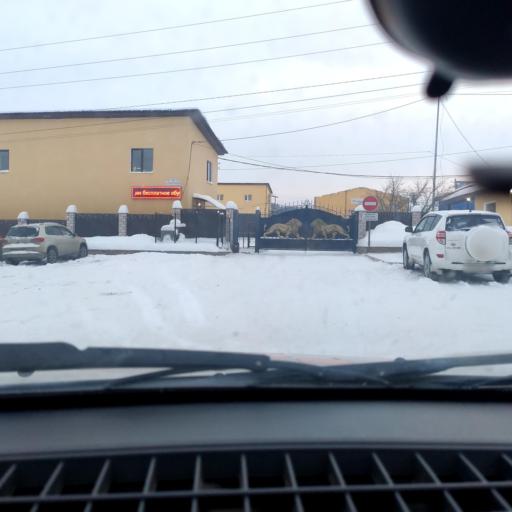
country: RU
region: Bashkortostan
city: Ufa
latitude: 54.5352
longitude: 55.9116
